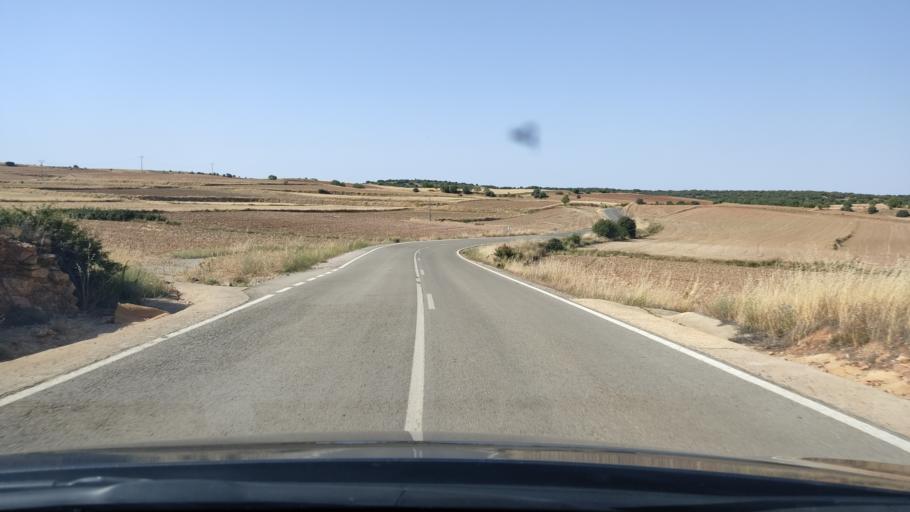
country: ES
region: Aragon
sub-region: Provincia de Teruel
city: Cucalon
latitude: 41.0797
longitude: -1.2230
